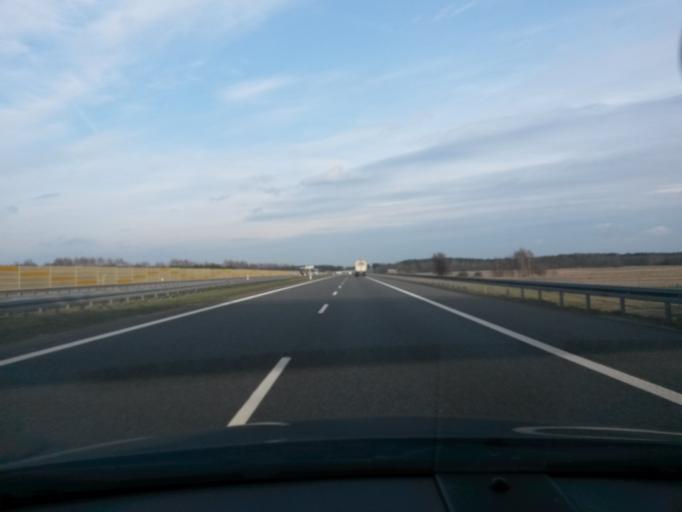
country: PL
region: Lodz Voivodeship
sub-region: Powiat zgierski
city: Parzeczew
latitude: 51.9376
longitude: 19.2486
